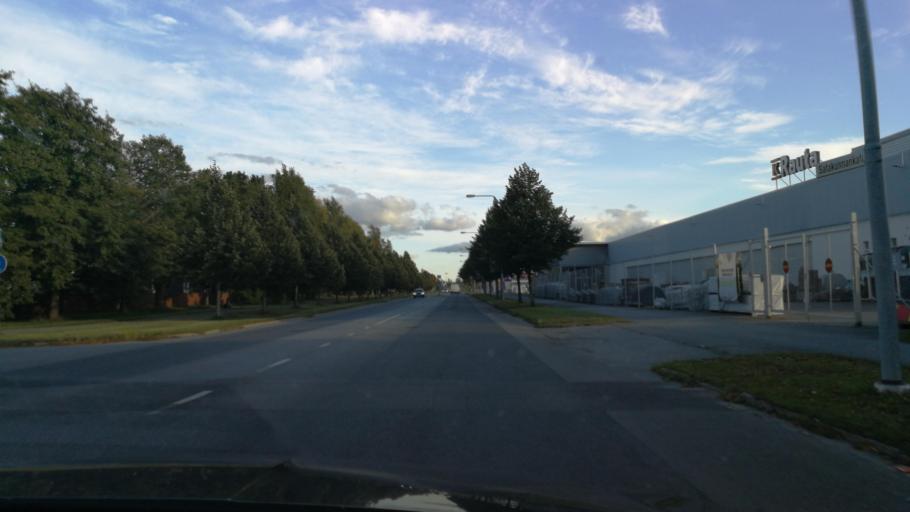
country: FI
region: Satakunta
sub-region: Pori
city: Pori
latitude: 61.4712
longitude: 21.8031
